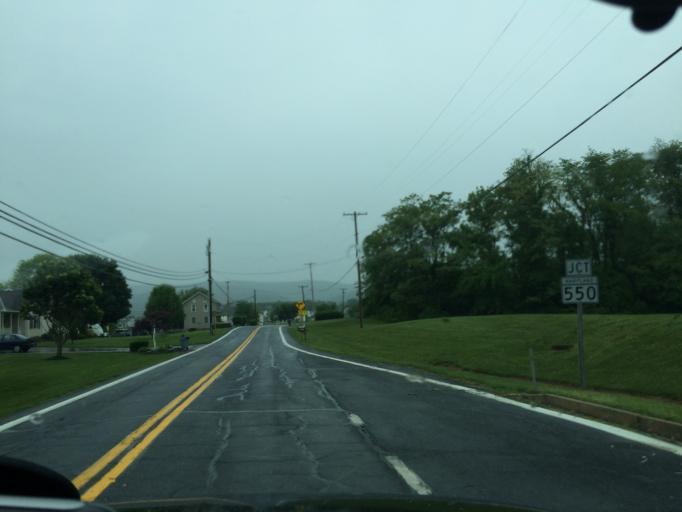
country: US
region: Maryland
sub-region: Frederick County
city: Thurmont
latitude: 39.6152
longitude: -77.3946
